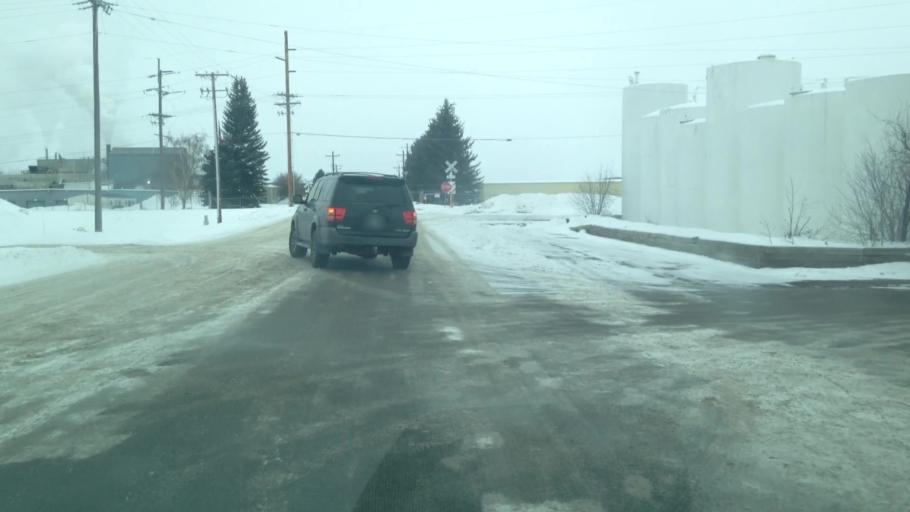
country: US
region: Idaho
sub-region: Madison County
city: Rexburg
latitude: 43.8404
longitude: -111.7786
